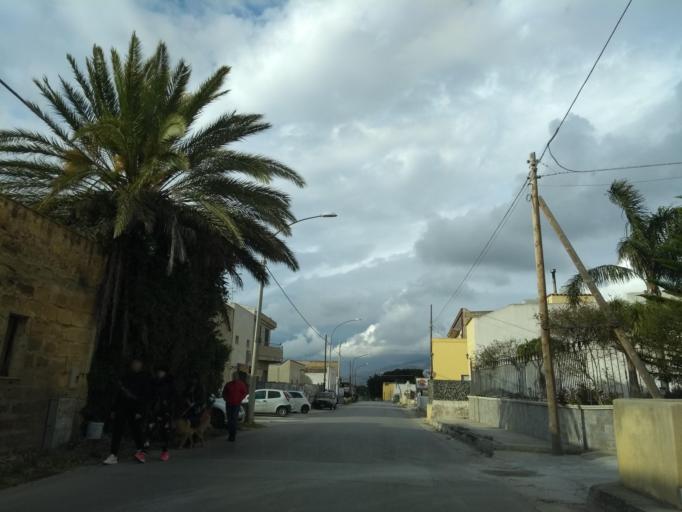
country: IT
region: Sicily
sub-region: Trapani
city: Marausa
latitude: 37.9523
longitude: 12.5150
